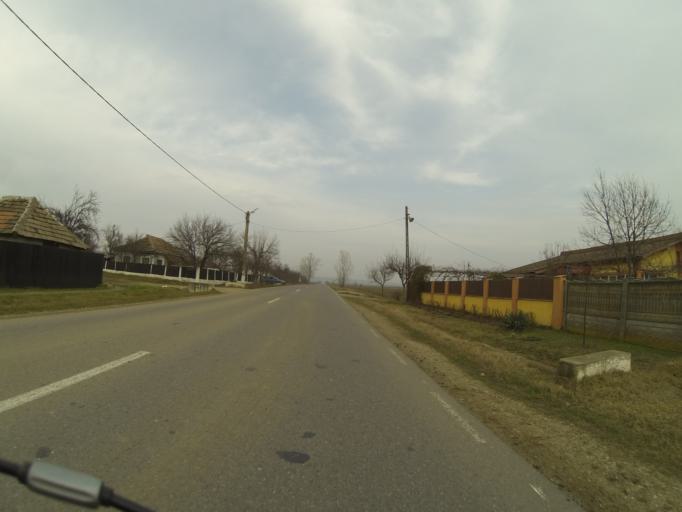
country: RO
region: Mehedinti
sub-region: Comuna Corlatel
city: Corlatel
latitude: 44.4026
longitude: 22.9382
